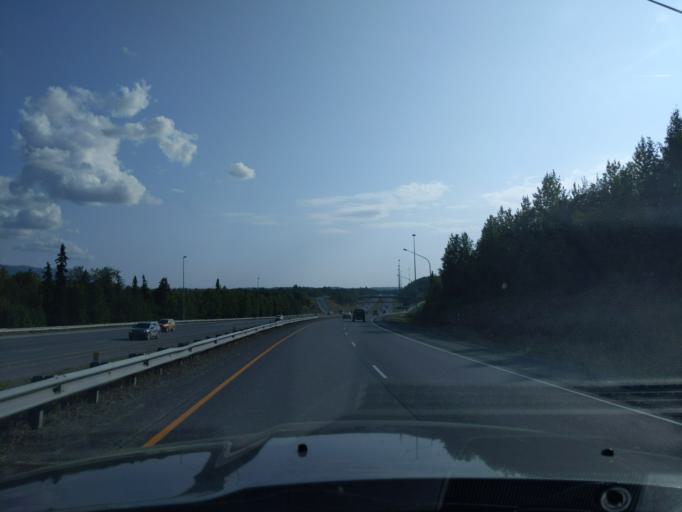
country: US
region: Alaska
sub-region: Anchorage Municipality
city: Eagle River
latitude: 61.3476
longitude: -149.5551
